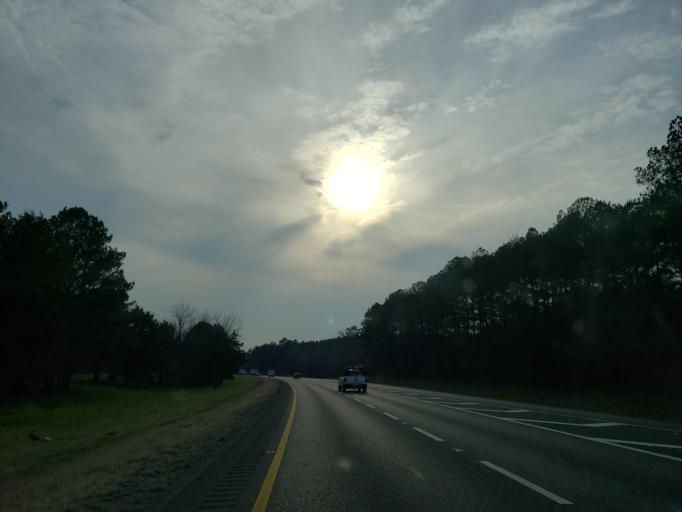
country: US
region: Tennessee
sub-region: Bradley County
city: Hopewell
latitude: 35.3243
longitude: -84.7863
